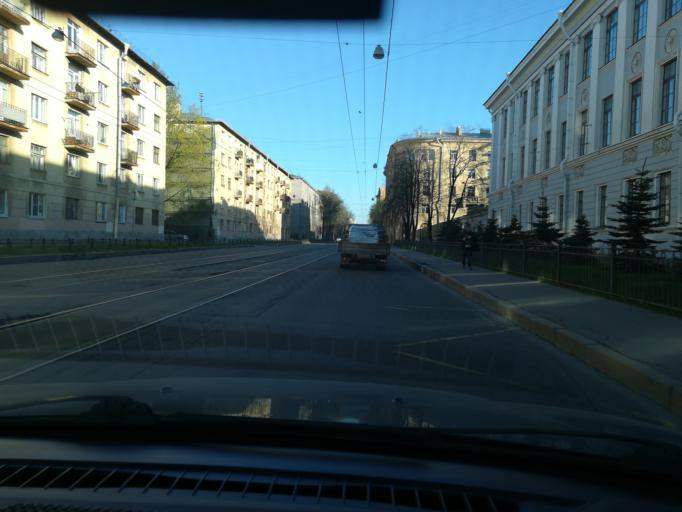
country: RU
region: St.-Petersburg
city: Vasyl'evsky Ostrov
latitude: 59.9365
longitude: 30.2588
